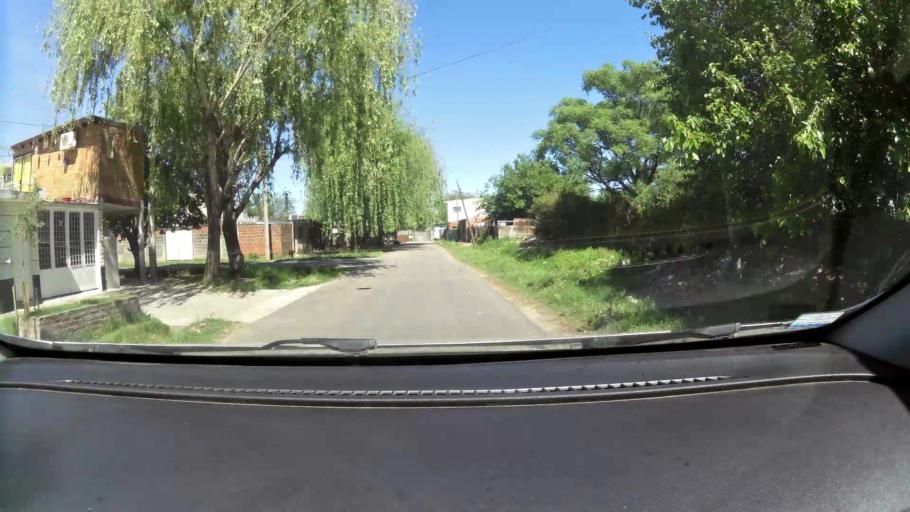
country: AR
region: Santa Fe
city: Perez
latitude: -32.9725
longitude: -60.7123
